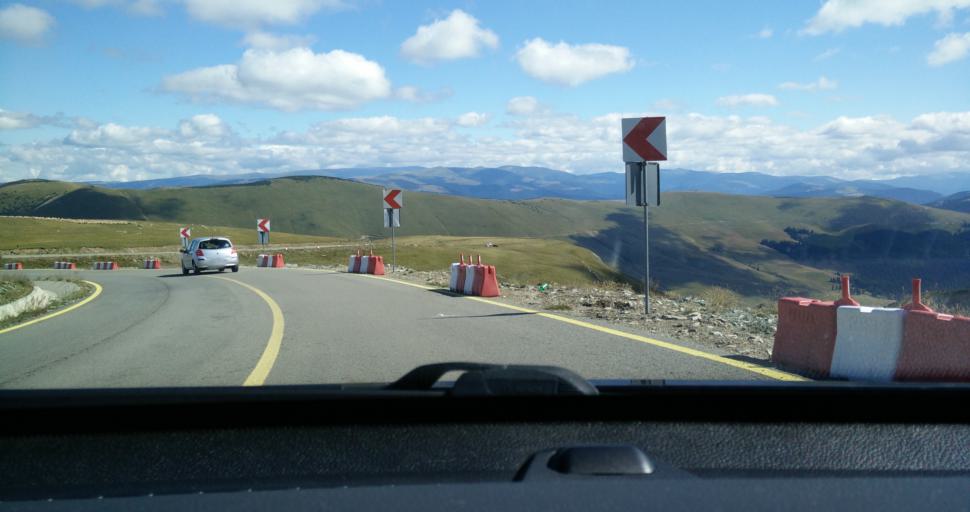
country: RO
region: Gorj
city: Novaci-Straini
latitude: 45.3671
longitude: 23.6510
